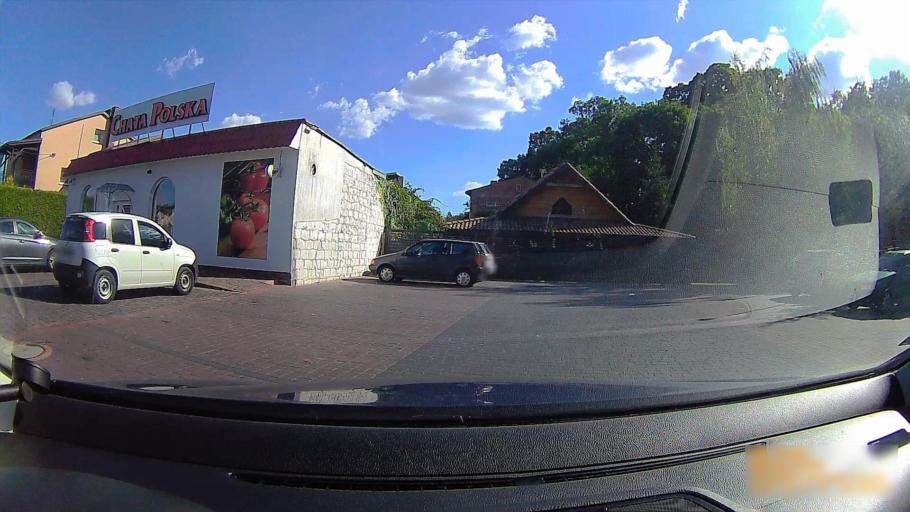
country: PL
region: Greater Poland Voivodeship
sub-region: Konin
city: Konin
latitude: 52.1973
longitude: 18.3030
